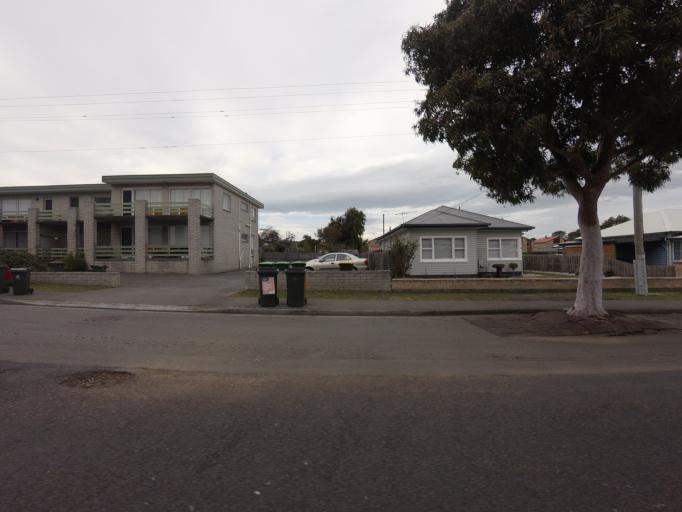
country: AU
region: Tasmania
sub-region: Clarence
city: Bellerive
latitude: -42.8773
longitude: 147.3789
